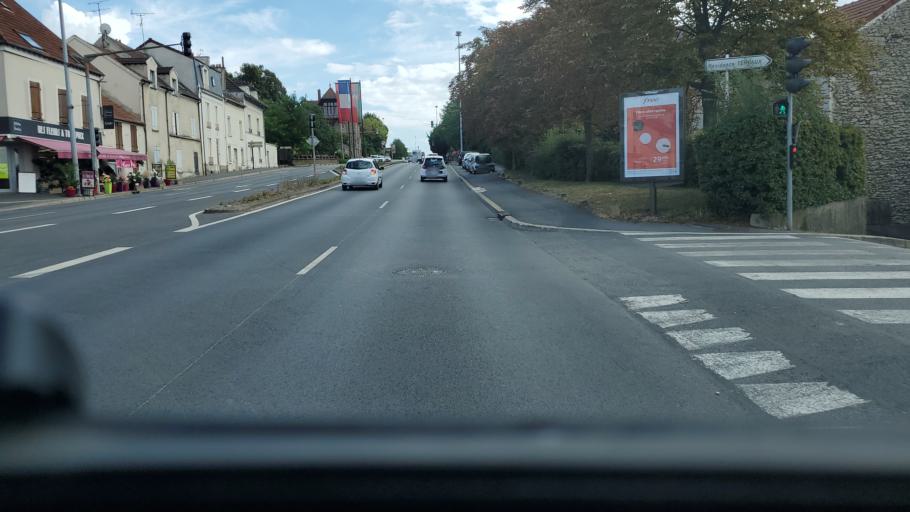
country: FR
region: Ile-de-France
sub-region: Departement de Seine-et-Marne
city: Meaux
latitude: 48.9519
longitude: 2.8796
